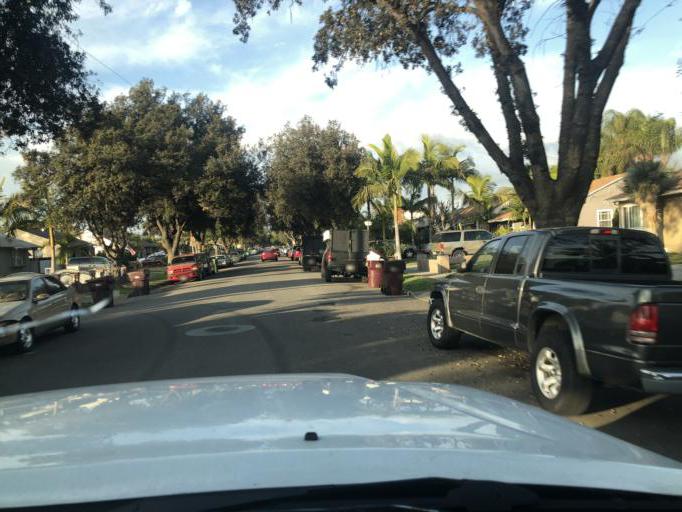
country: US
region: California
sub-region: Orange County
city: Santa Ana
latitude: 33.7170
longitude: -117.8740
